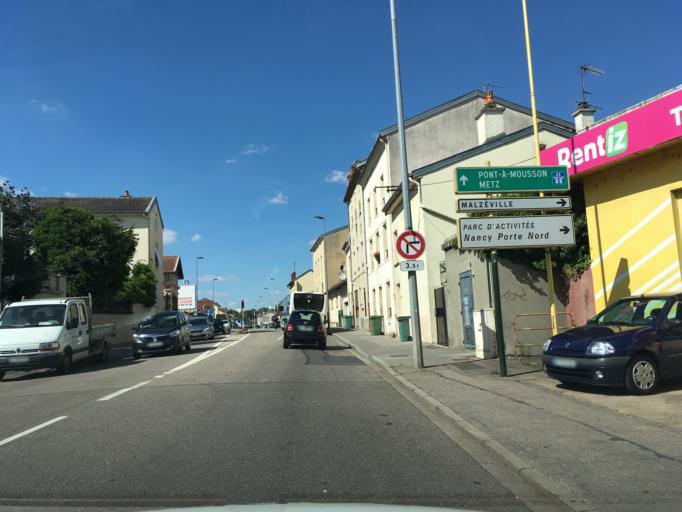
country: FR
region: Lorraine
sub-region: Departement de Meurthe-et-Moselle
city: Maxeville
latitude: 48.7118
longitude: 6.1679
